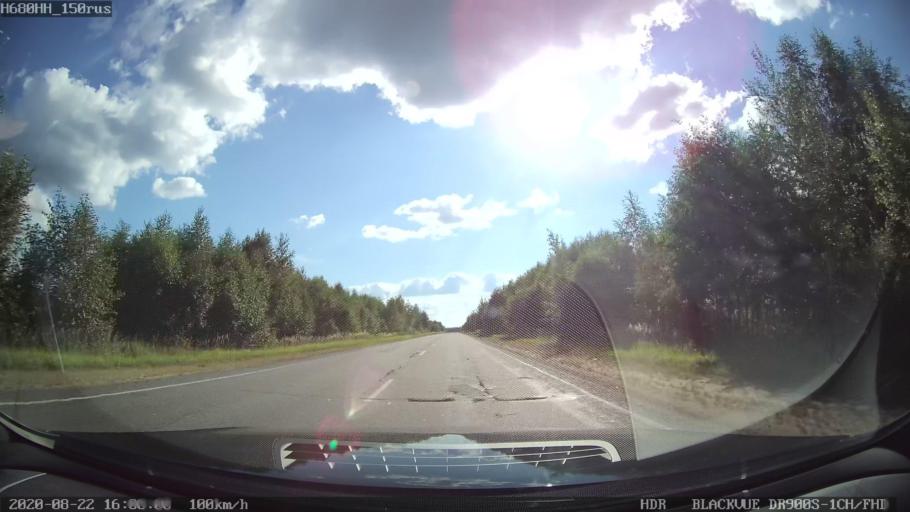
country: RU
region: Tverskaya
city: Rameshki
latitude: 57.5453
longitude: 36.3055
